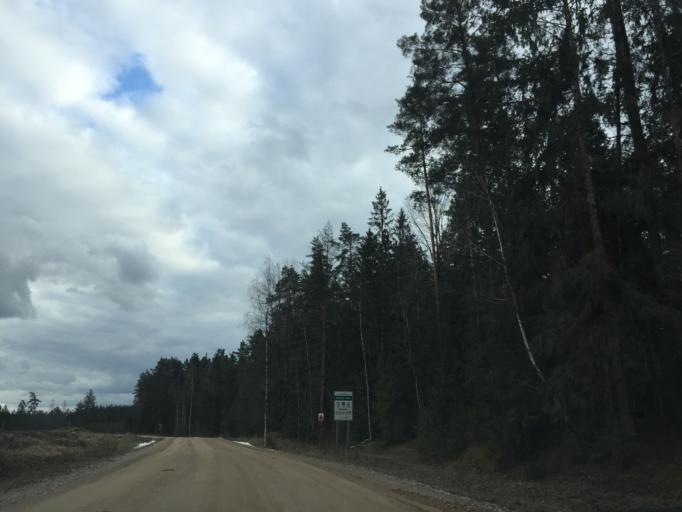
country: LV
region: Ogre
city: Jumprava
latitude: 56.5934
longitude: 24.9868
